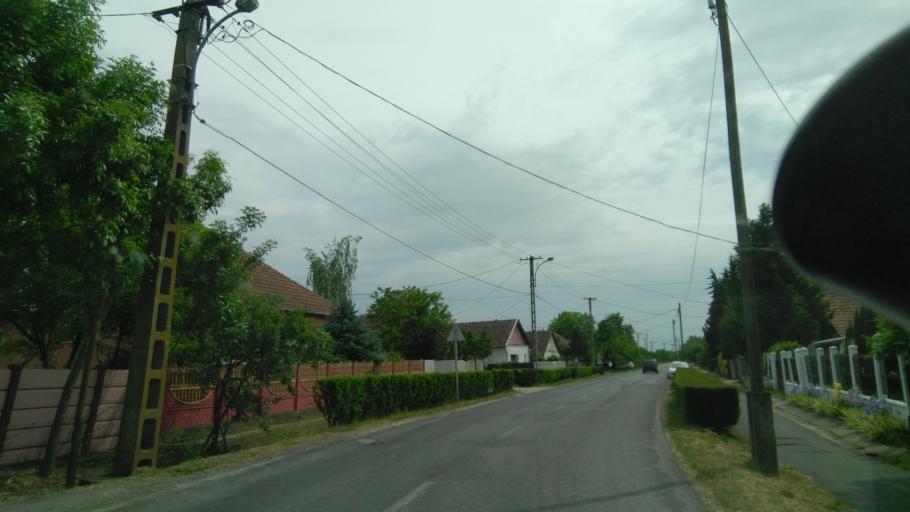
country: HU
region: Bekes
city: Sarkad
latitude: 46.8011
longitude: 21.3851
